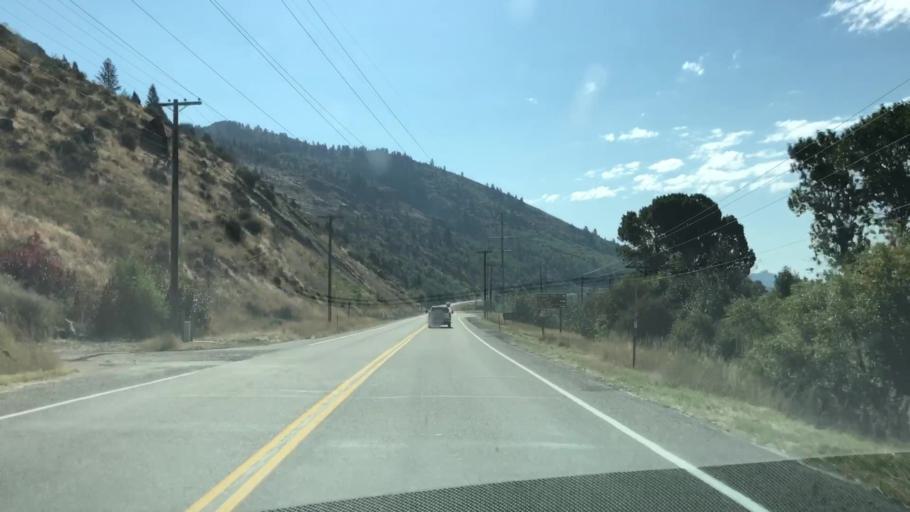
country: US
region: Idaho
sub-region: Teton County
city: Victor
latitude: 43.3466
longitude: -111.2094
